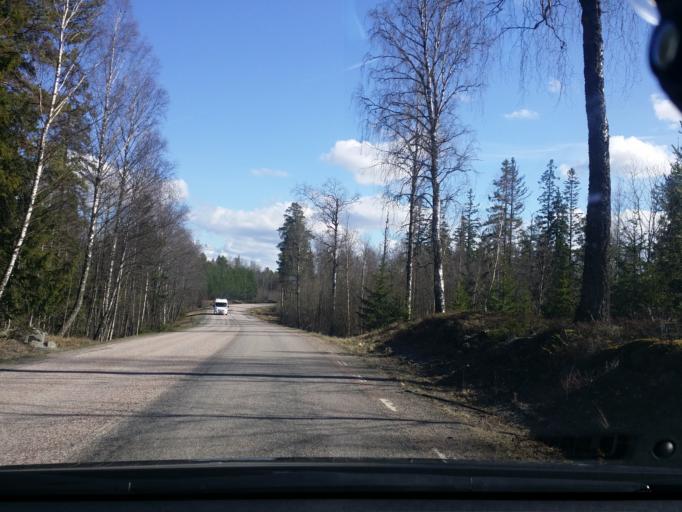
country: SE
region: Vaestmanland
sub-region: Sala Kommun
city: Sala
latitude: 59.9733
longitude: 16.4991
